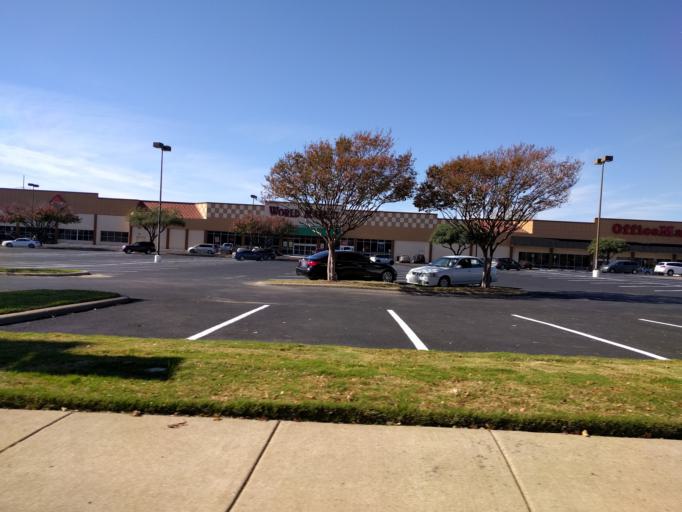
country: US
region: Texas
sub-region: Collin County
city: Plano
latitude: 33.0186
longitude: -96.7096
